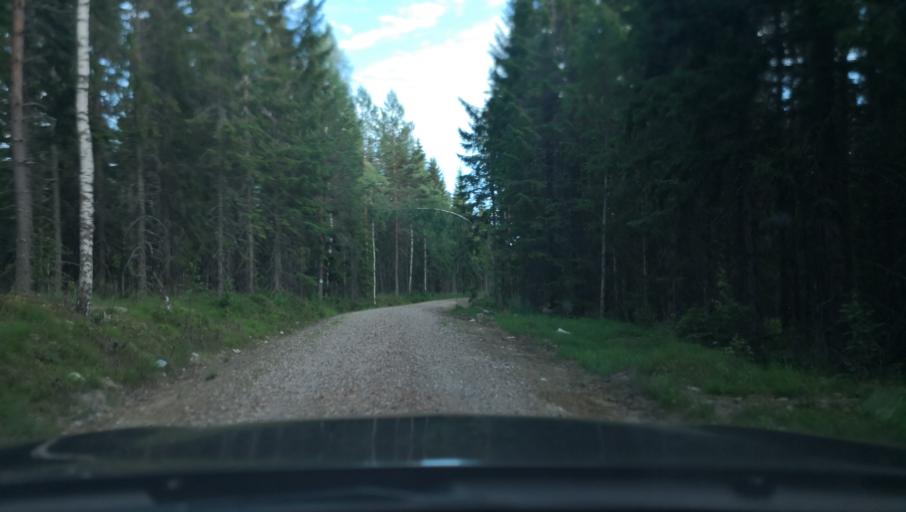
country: SE
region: Dalarna
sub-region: Ludvika Kommun
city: Ludvika
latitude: 60.0754
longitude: 15.2898
